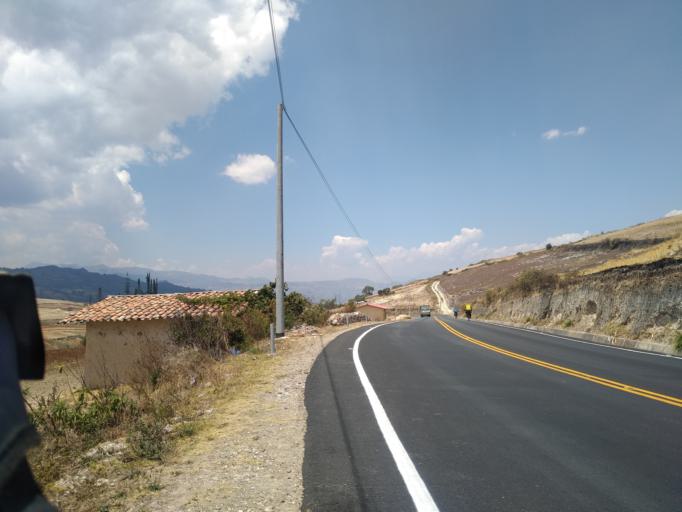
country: PE
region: Cajamarca
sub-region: San Marcos
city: San Marcos
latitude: -7.2745
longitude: -78.2476
